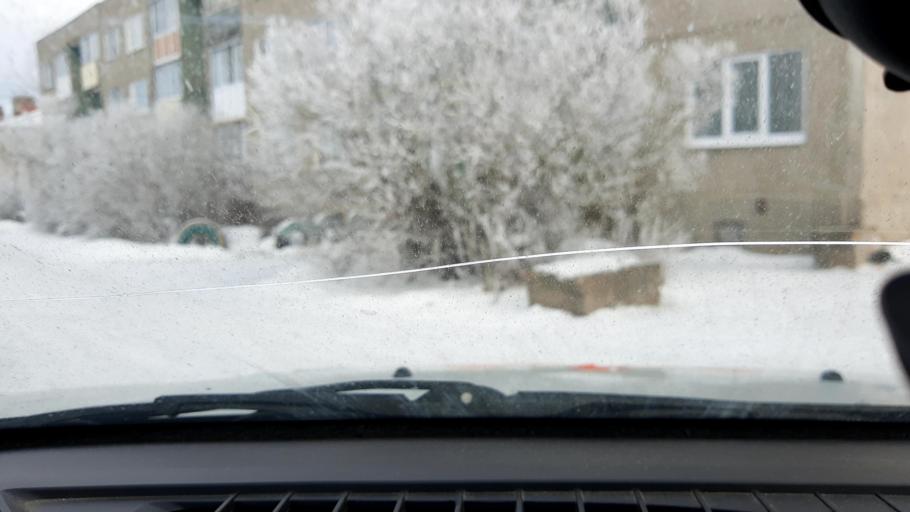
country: RU
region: Nizjnij Novgorod
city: Bogorodsk
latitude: 56.0355
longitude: 43.6217
